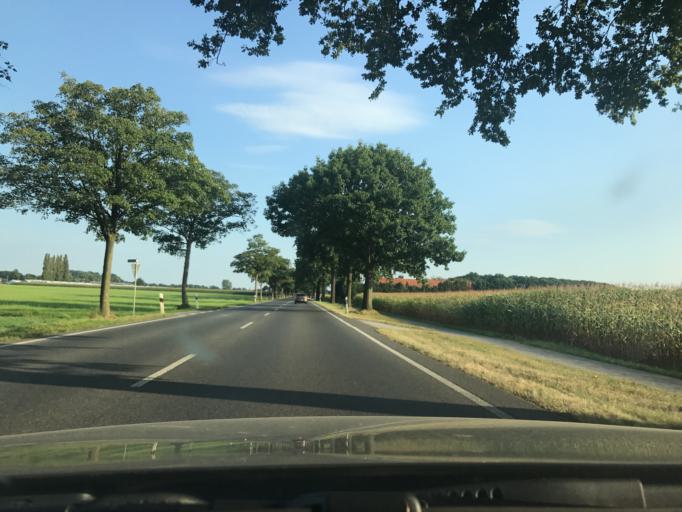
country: DE
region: North Rhine-Westphalia
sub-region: Regierungsbezirk Dusseldorf
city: Kevelaer
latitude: 51.5402
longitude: 6.2723
